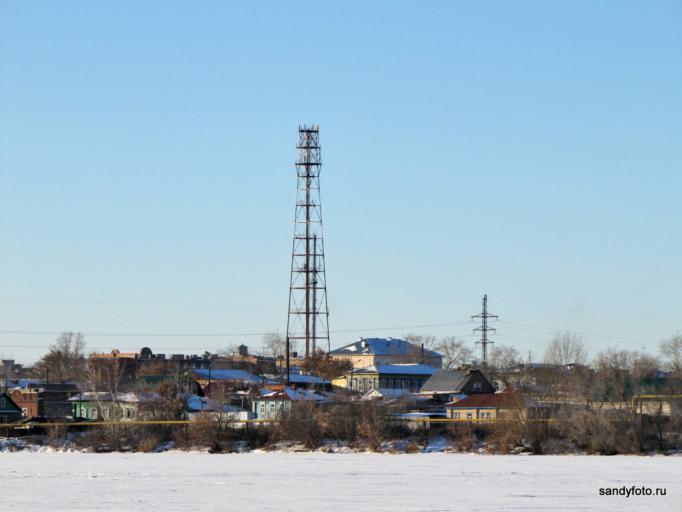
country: RU
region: Chelyabinsk
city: Troitsk
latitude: 54.0789
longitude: 61.5727
